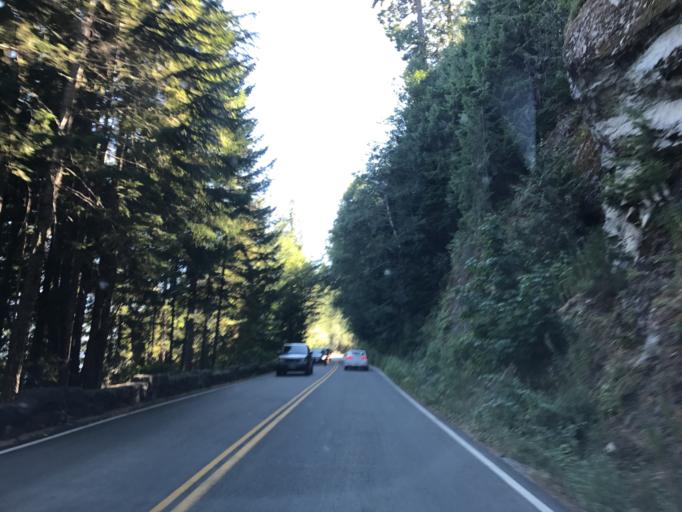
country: US
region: Washington
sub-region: Pierce County
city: Buckley
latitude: 46.7375
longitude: -121.5790
